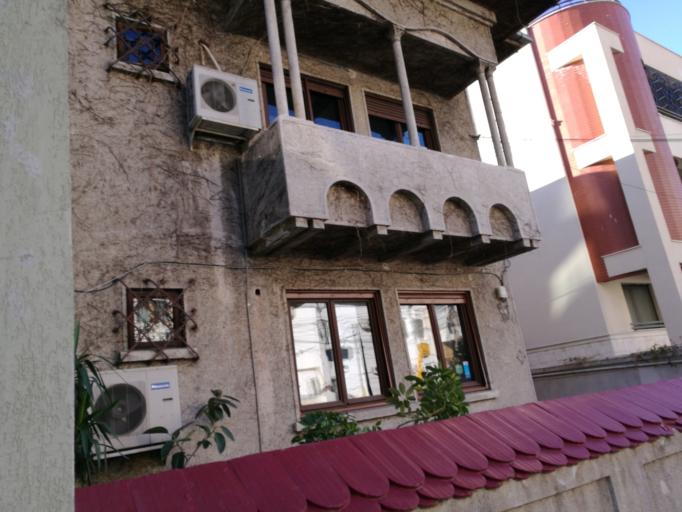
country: RO
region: Bucuresti
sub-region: Municipiul Bucuresti
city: Bucuresti
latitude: 44.4626
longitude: 26.0850
